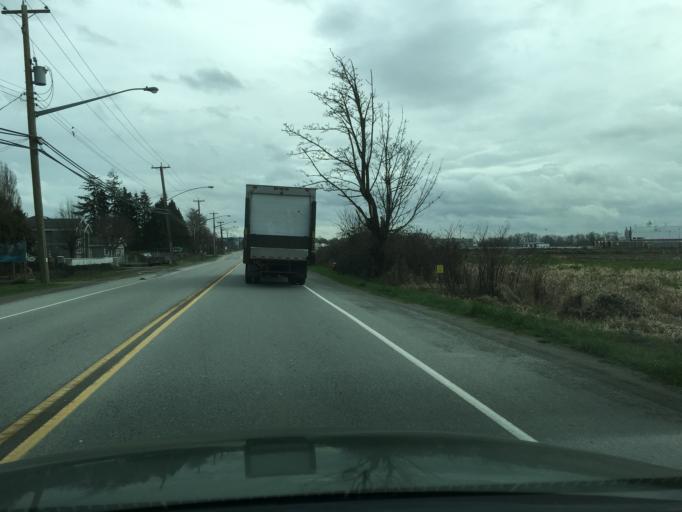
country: CA
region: British Columbia
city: Ladner
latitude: 49.1335
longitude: -123.0777
